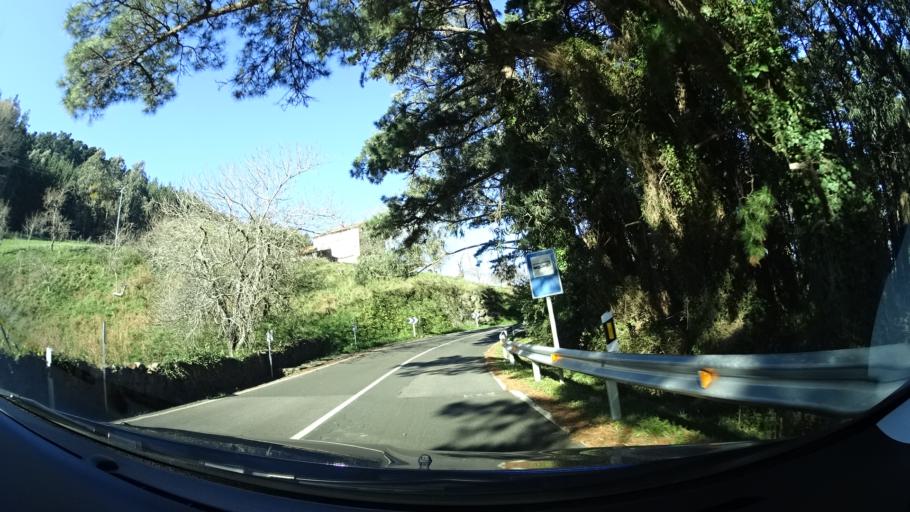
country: ES
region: Basque Country
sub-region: Bizkaia
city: Bermeo
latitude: 43.4377
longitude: -2.7497
